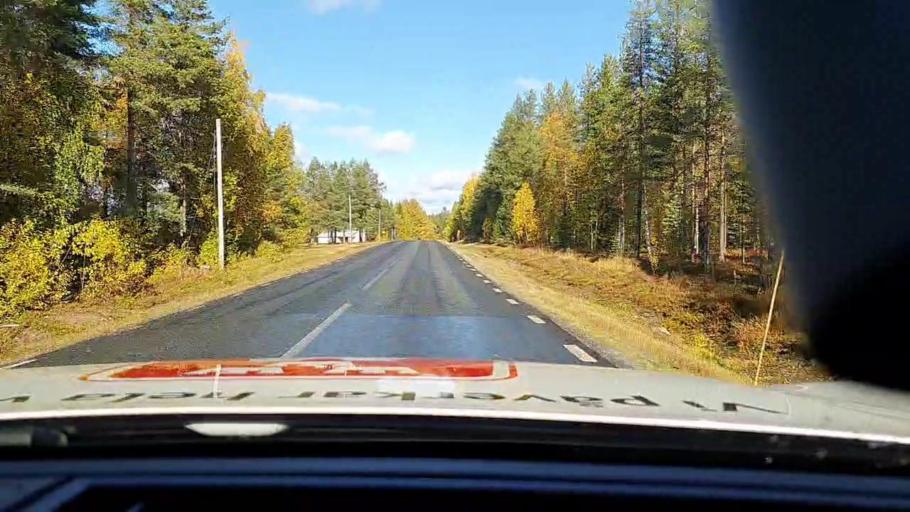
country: SE
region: Vaesterbotten
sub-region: Skelleftea Kommun
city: Langsele
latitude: 64.9981
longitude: 20.0904
